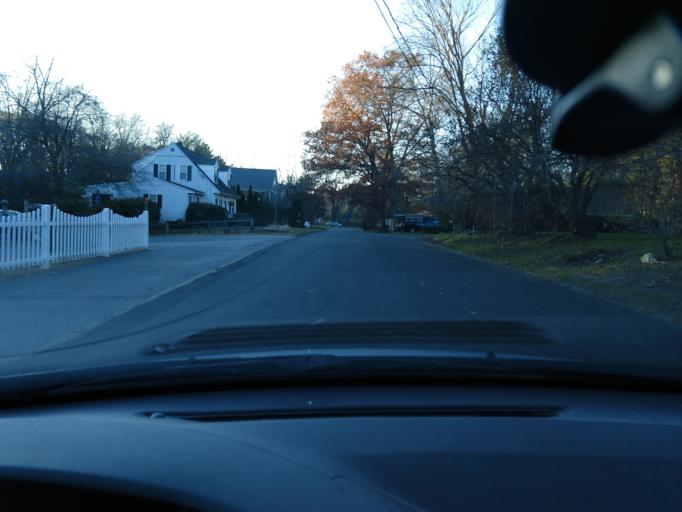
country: US
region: Massachusetts
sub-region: Middlesex County
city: Bedford
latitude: 42.4873
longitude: -71.2711
